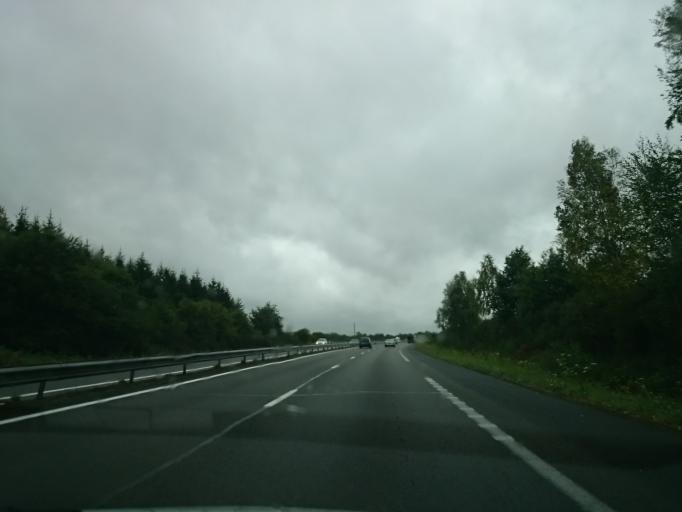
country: FR
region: Pays de la Loire
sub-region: Departement de la Loire-Atlantique
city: Treillieres
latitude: 47.3037
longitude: -1.6332
